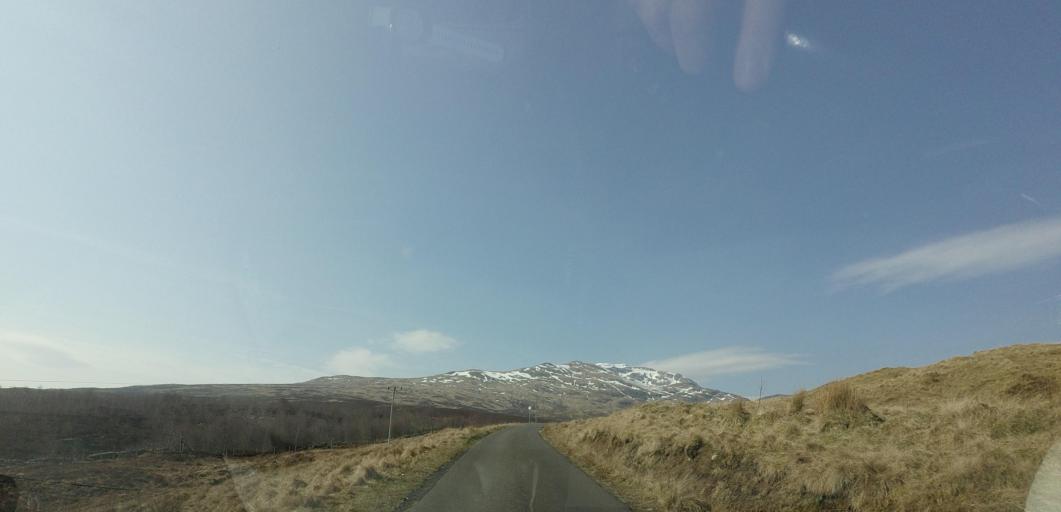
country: GB
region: Scotland
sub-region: Stirling
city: Callander
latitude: 56.5100
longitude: -4.2582
